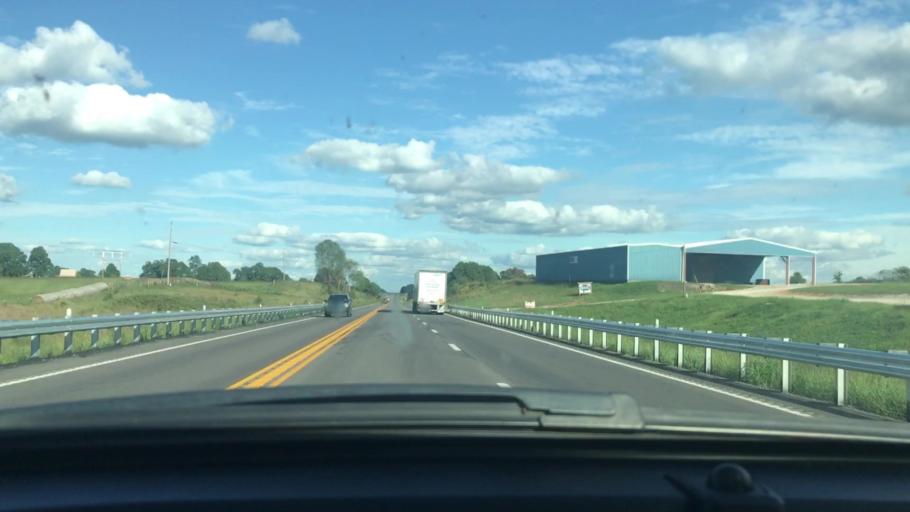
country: US
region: Missouri
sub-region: Oregon County
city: Thayer
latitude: 36.5881
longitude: -91.6348
